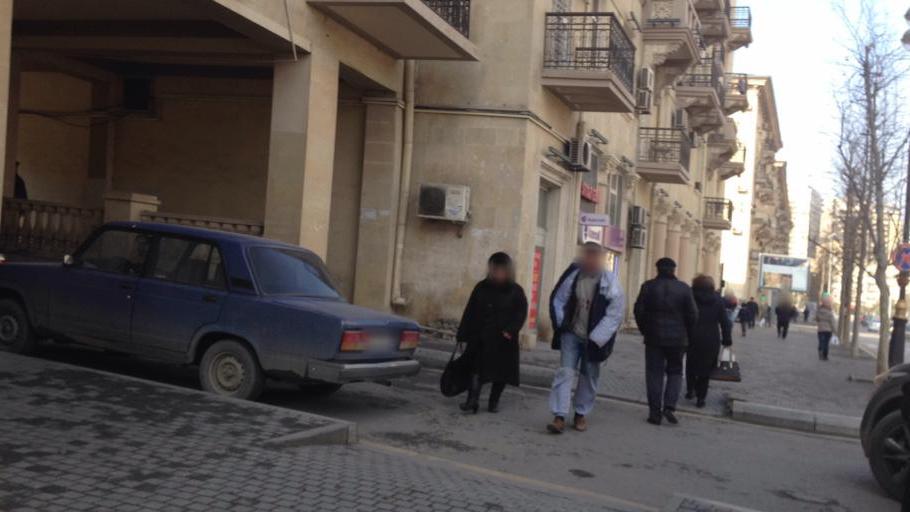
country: AZ
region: Baki
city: Badamdar
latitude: 40.3728
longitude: 49.8331
